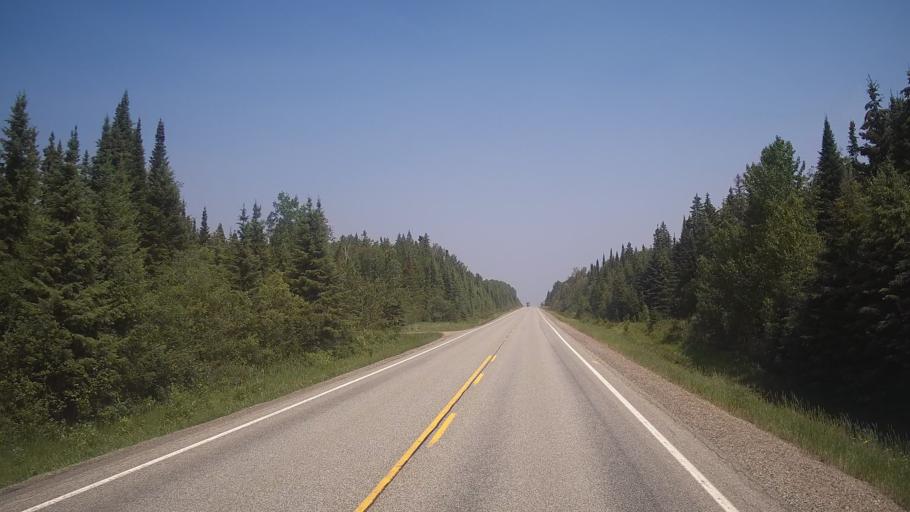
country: CA
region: Ontario
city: Timmins
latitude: 48.1964
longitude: -81.5815
